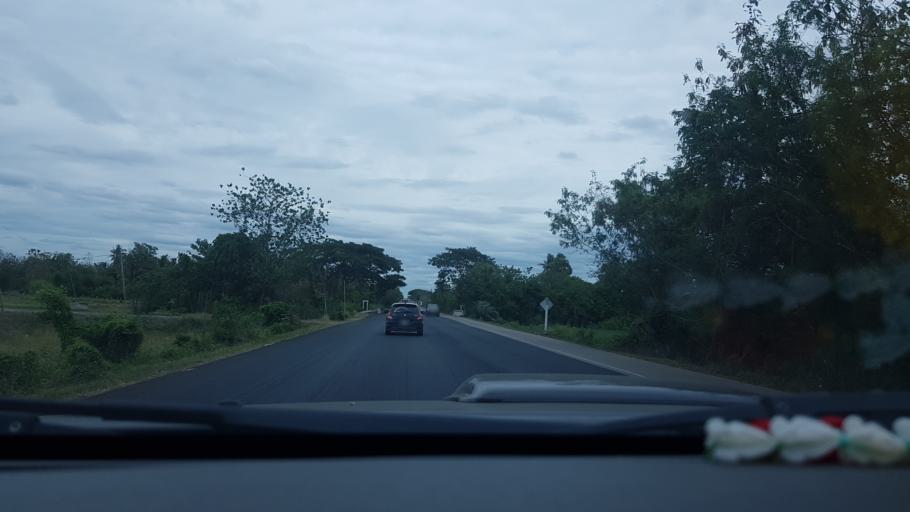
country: TH
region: Phetchabun
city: Phetchabun
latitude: 16.4613
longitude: 101.1210
